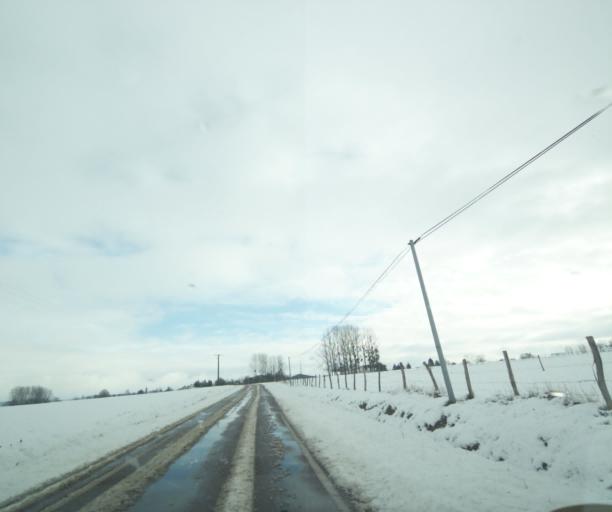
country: FR
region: Champagne-Ardenne
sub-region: Departement de la Haute-Marne
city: Montier-en-Der
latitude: 48.4540
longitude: 4.6665
